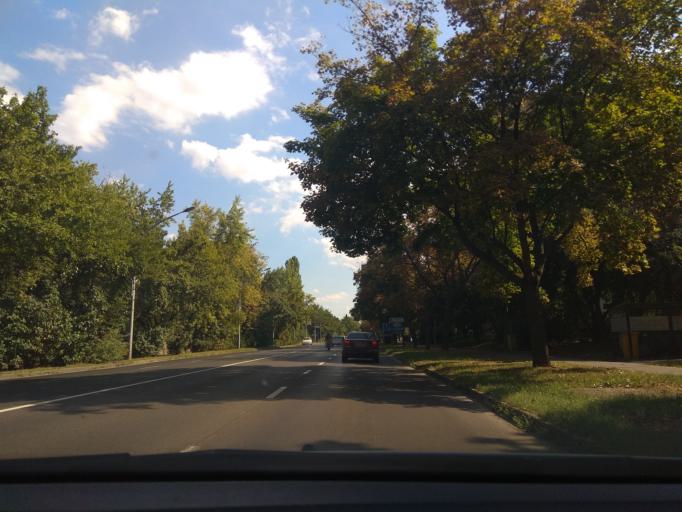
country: HU
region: Borsod-Abauj-Zemplen
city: Miskolc
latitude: 48.1187
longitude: 20.7887
